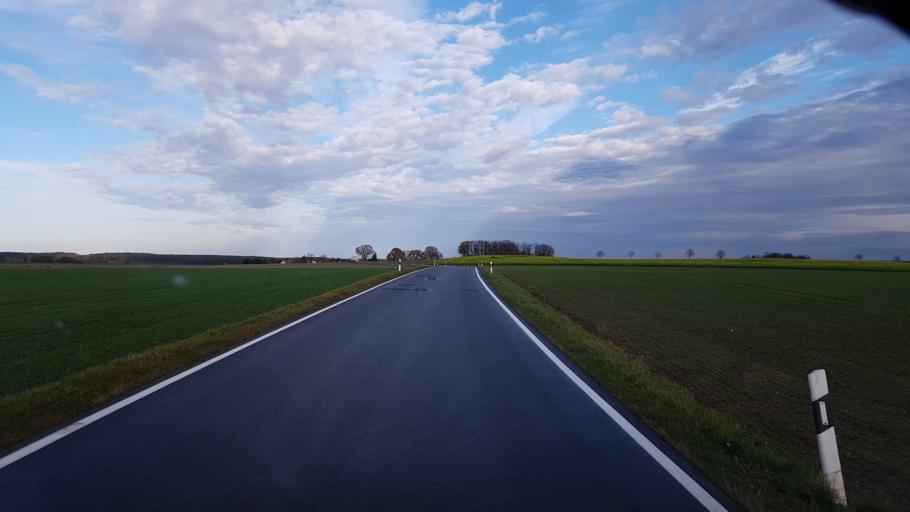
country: DE
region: Brandenburg
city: Ortrand
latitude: 51.3338
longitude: 13.7578
